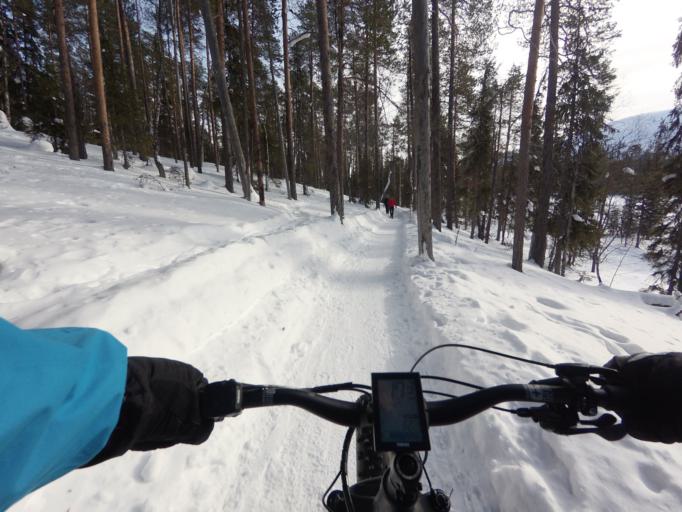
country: FI
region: Lapland
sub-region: Tunturi-Lappi
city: Kolari
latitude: 67.6003
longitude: 24.2452
